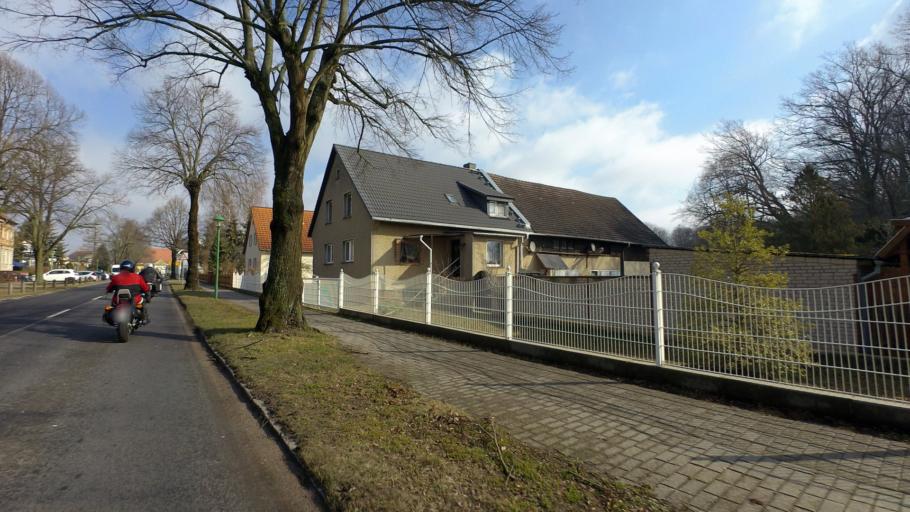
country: DE
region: Brandenburg
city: Glienicke
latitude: 52.6537
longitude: 13.3392
